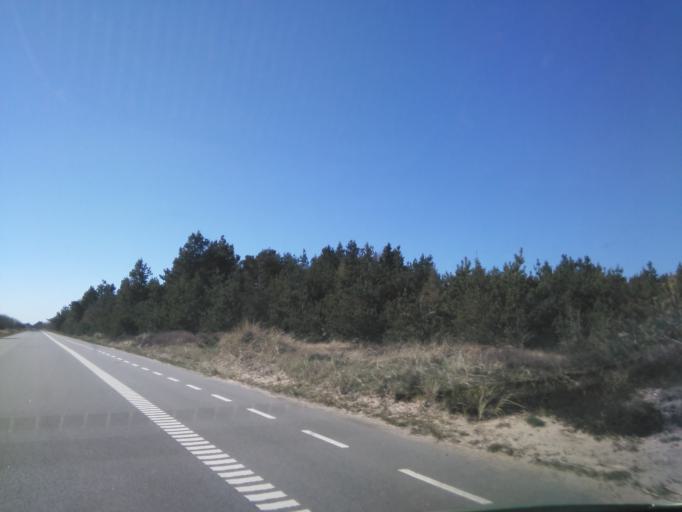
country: DK
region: South Denmark
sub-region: Varde Kommune
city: Oksbol
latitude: 55.5507
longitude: 8.2012
